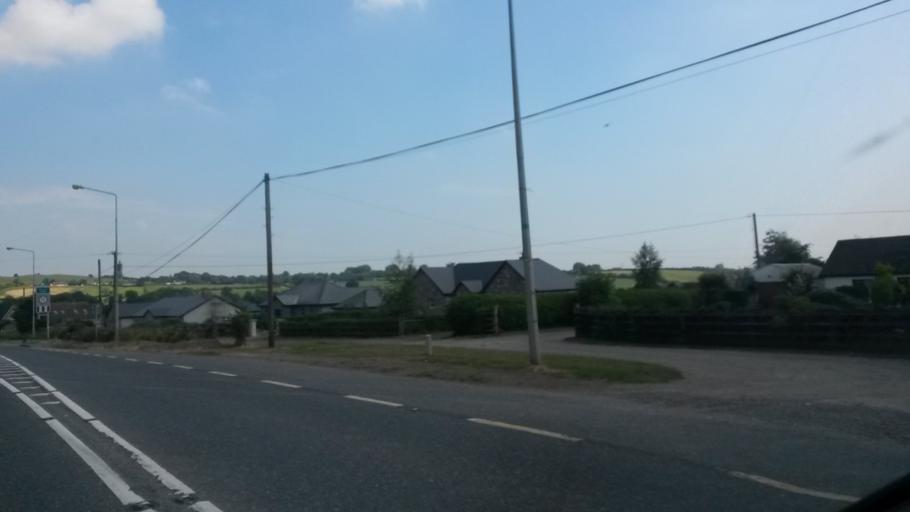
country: IE
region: Leinster
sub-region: An Mhi
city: Slane
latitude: 53.6977
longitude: -6.5383
